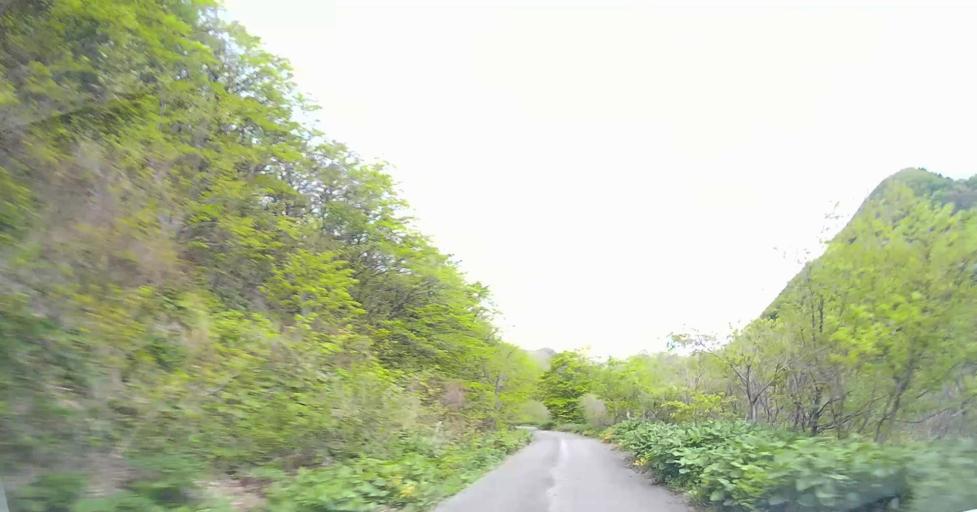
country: JP
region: Aomori
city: Shimokizukuri
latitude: 41.2373
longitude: 140.3455
